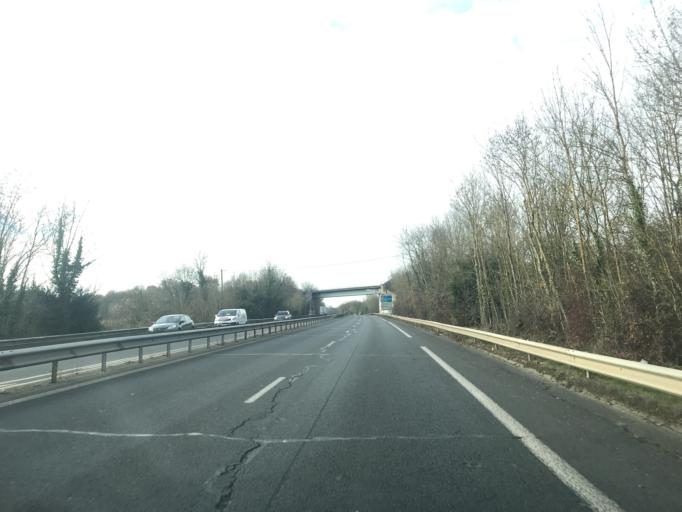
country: FR
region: Poitou-Charentes
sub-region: Departement des Deux-Sevres
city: Niort
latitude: 46.3351
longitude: -0.4382
